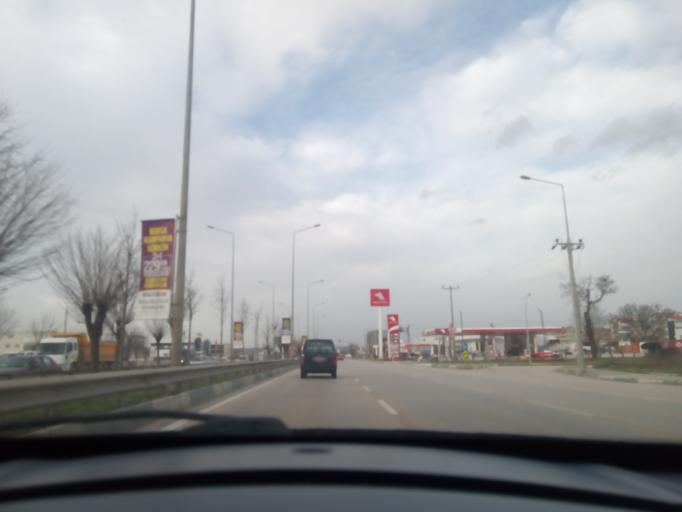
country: TR
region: Bursa
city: Cali
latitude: 40.2140
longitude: 28.9120
